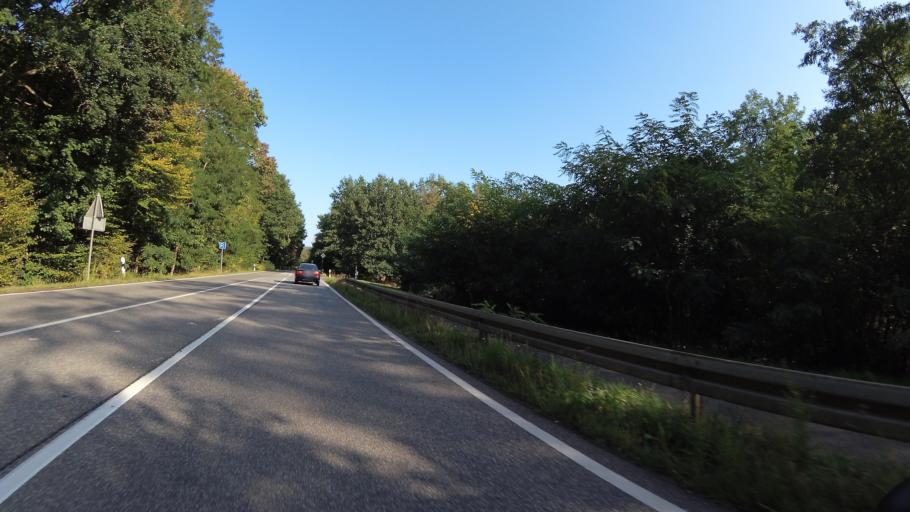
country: DE
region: Saarland
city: Sankt Ingbert
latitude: 49.2666
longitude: 7.1410
